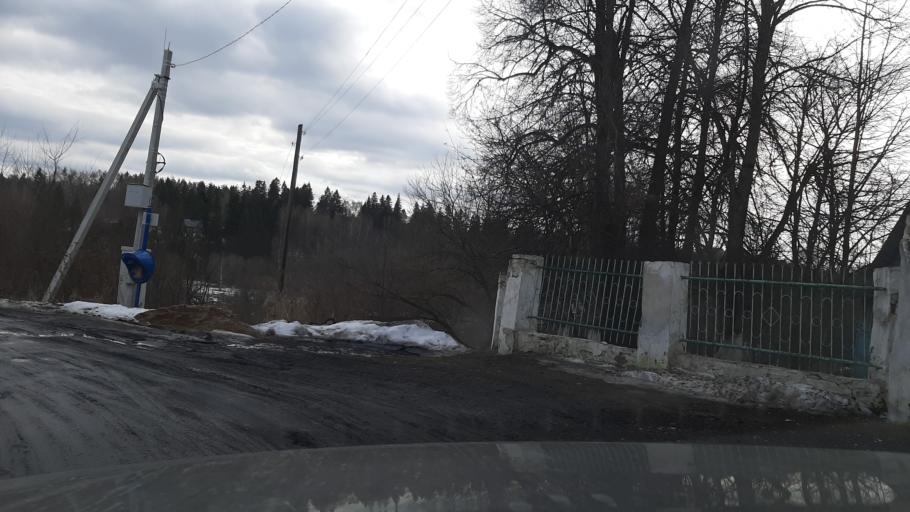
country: RU
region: Ivanovo
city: Teykovo
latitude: 56.8970
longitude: 40.6639
